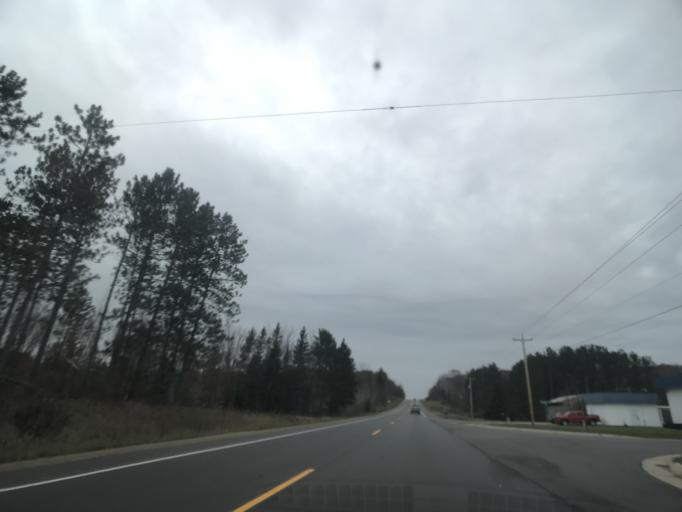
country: US
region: Wisconsin
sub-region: Menominee County
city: Legend Lake
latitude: 45.2419
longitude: -88.5154
